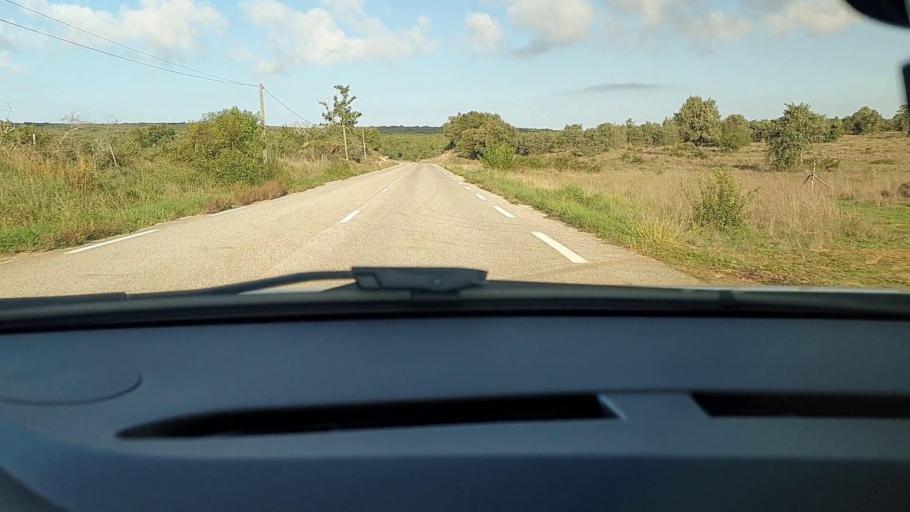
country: FR
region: Languedoc-Roussillon
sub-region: Departement du Gard
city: Barjac
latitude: 44.2154
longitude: 4.3305
